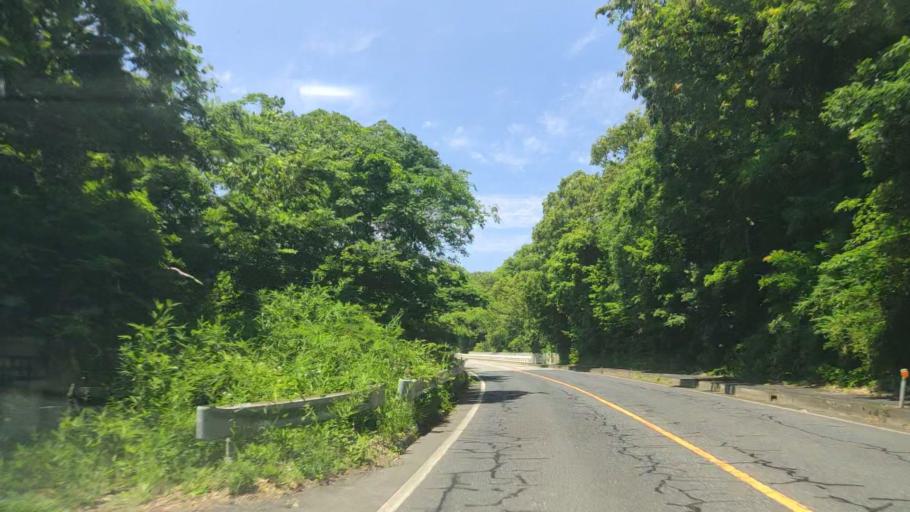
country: JP
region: Tottori
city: Tottori
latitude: 35.5278
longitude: 134.2300
